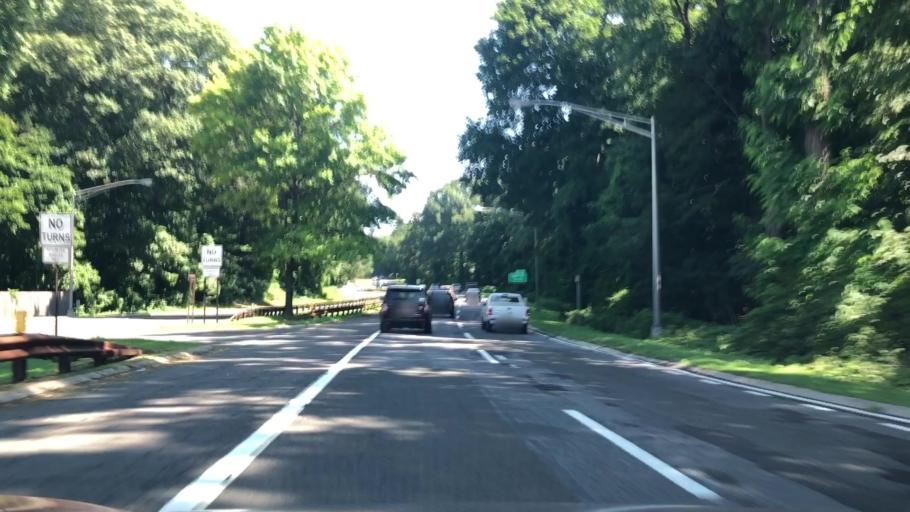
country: US
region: New York
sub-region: Westchester County
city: Greenville
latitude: 40.9941
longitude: -73.8058
